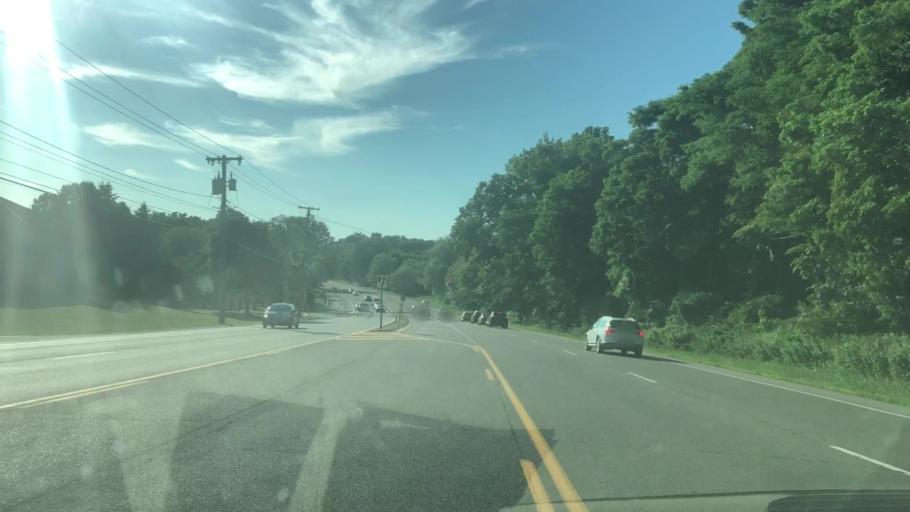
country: US
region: New York
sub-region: Ontario County
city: Victor
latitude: 43.0343
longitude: -77.4443
